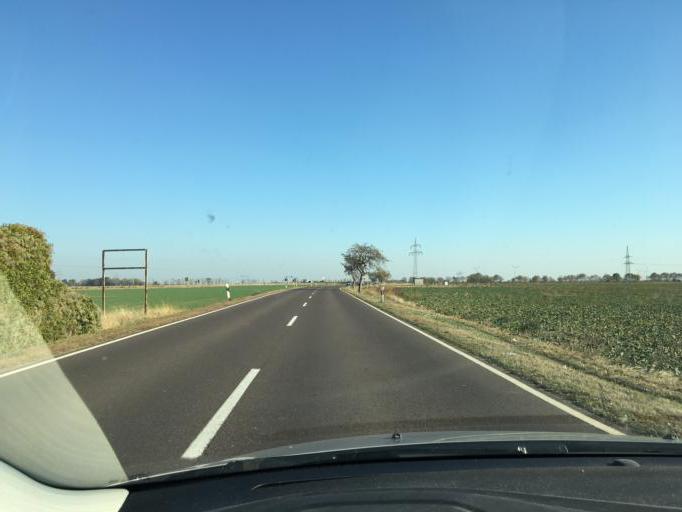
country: DE
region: Saxony-Anhalt
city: Baalberge
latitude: 51.7986
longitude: 11.7861
